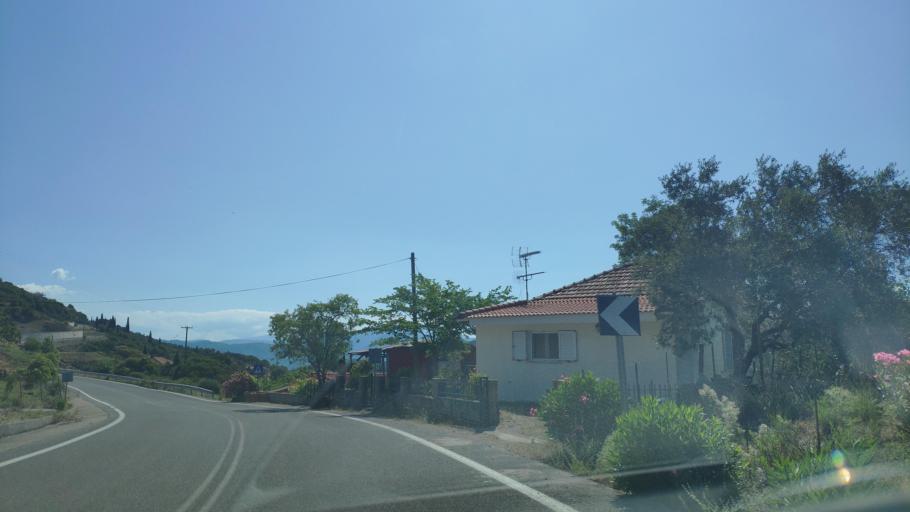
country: GR
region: Central Greece
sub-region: Nomos Evrytanias
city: Kerasochori
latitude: 38.9276
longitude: 21.4371
